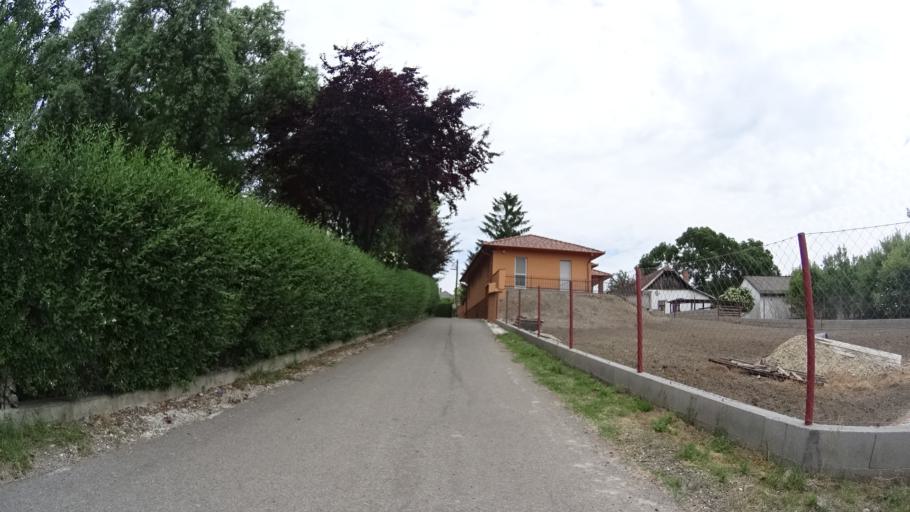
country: HU
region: Bacs-Kiskun
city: Tiszakecske
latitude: 46.9292
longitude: 20.0952
